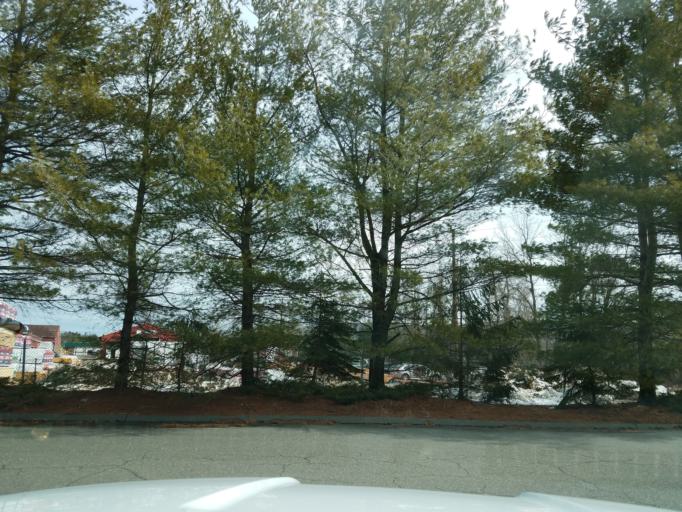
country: US
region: Connecticut
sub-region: Hartford County
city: Weatogue
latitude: 41.7976
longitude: -72.8380
